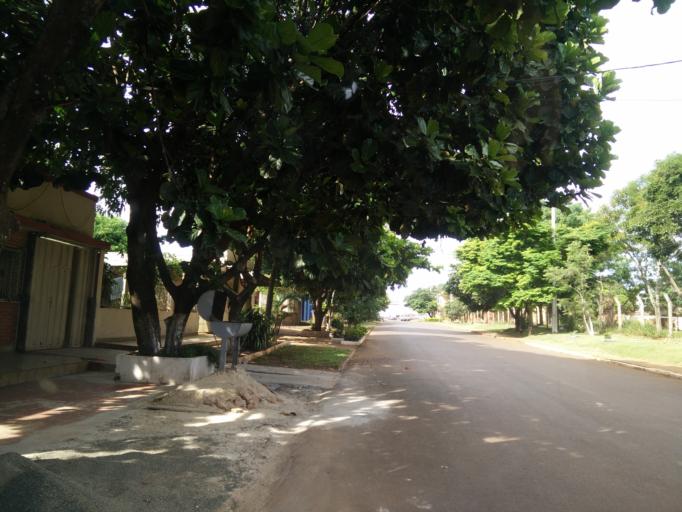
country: PY
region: Alto Parana
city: Ciudad del Este
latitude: -25.3925
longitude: -54.6404
